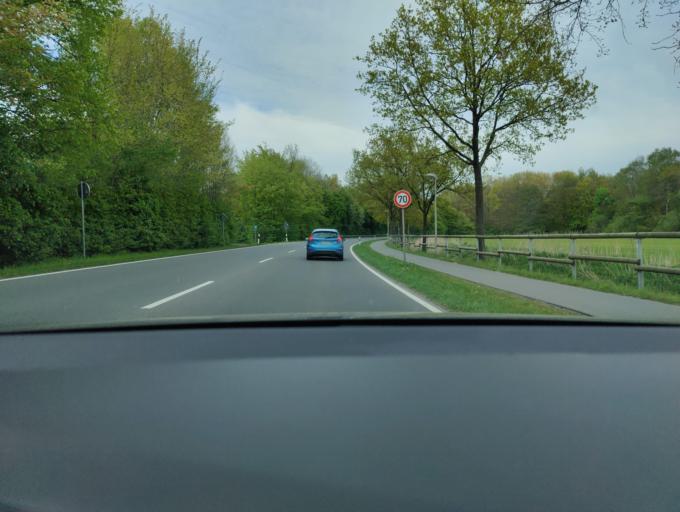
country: DE
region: North Rhine-Westphalia
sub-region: Regierungsbezirk Munster
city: Gronau
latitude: 52.2322
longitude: 7.0559
